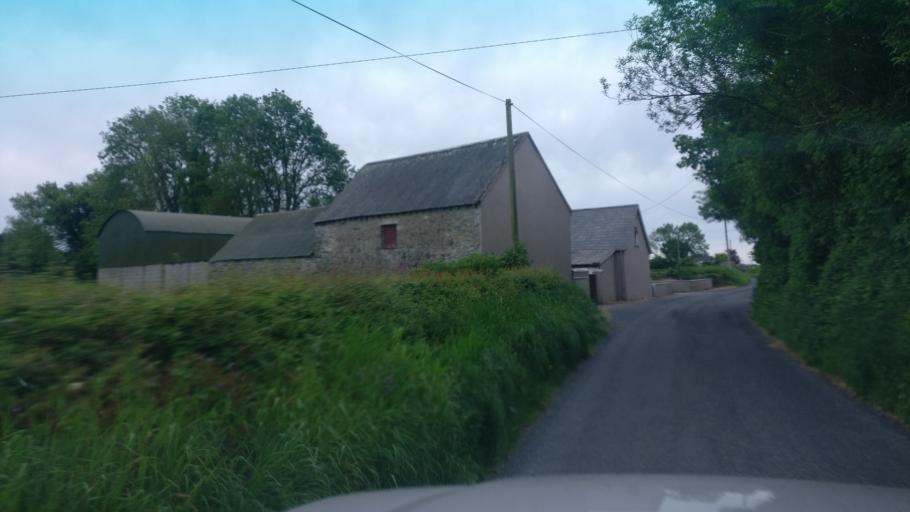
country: IE
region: Connaught
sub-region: County Galway
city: Portumna
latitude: 53.1201
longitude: -8.2898
